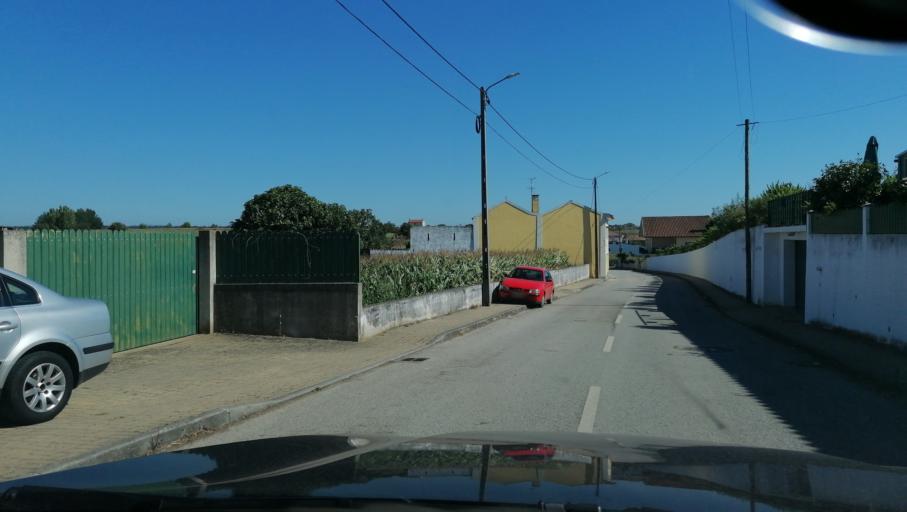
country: PT
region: Aveiro
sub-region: Estarreja
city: Salreu
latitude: 40.7480
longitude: -8.5482
